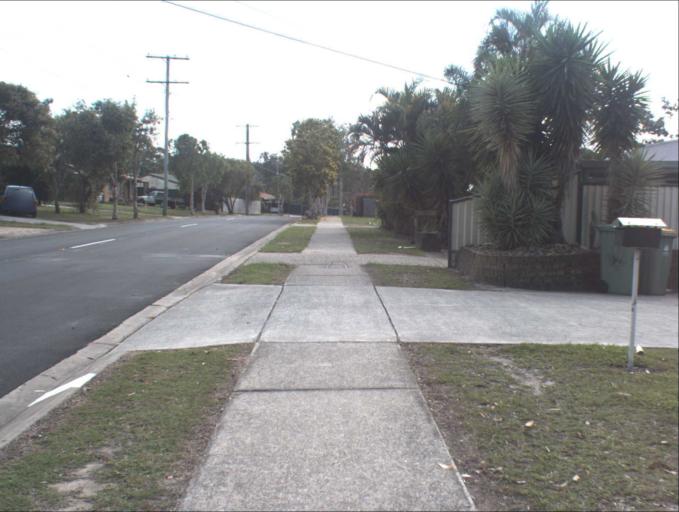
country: AU
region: Queensland
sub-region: Logan
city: Woodridge
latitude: -27.6678
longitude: 153.0652
